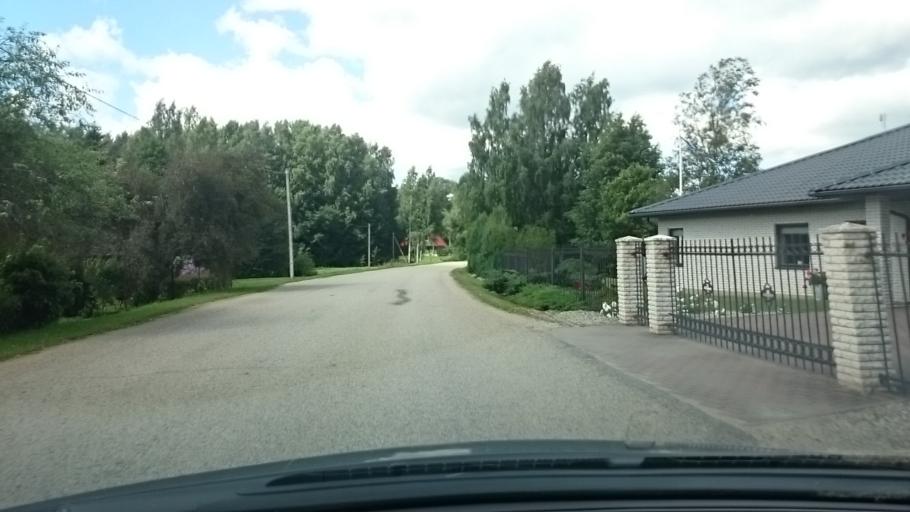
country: EE
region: Vorumaa
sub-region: Voru linn
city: Voru
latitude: 57.9239
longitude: 27.1204
